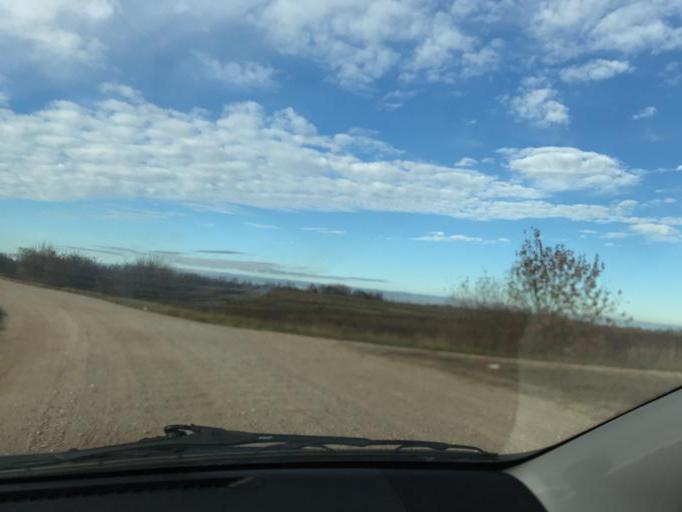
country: BY
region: Vitebsk
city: Haradok
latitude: 55.4540
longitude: 30.0331
